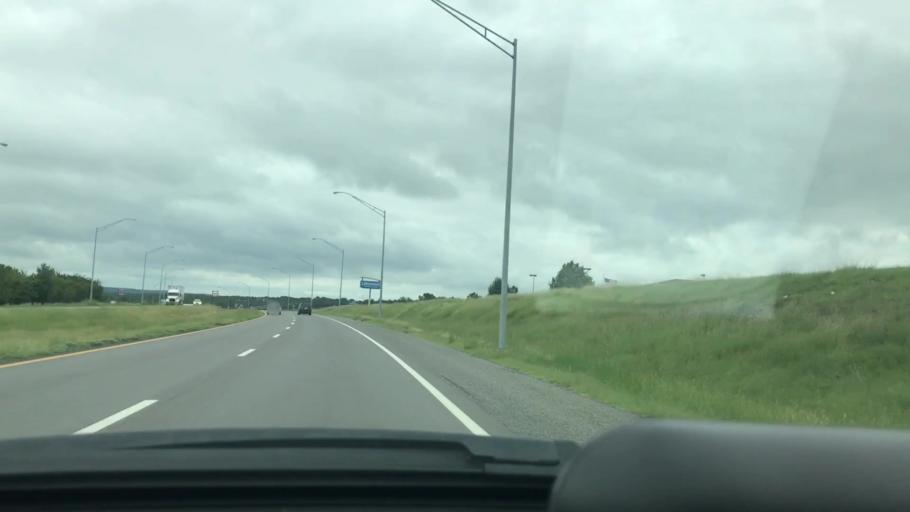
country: US
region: Oklahoma
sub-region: Pittsburg County
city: McAlester
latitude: 34.9006
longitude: -95.7521
